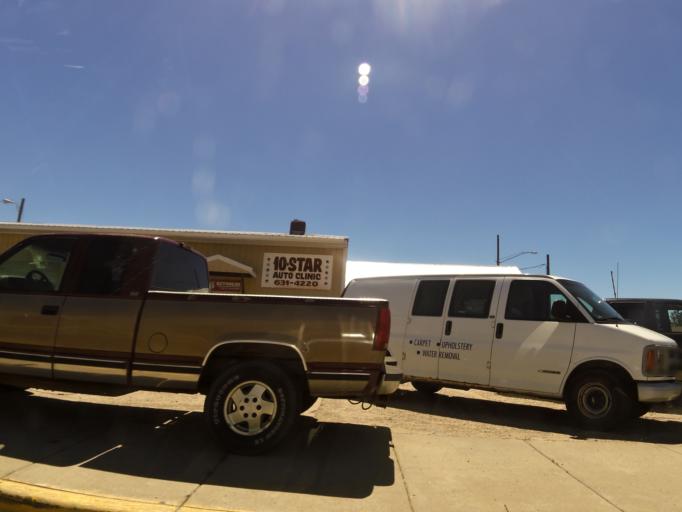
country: US
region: Minnesota
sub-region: Wadena County
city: Wadena
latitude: 46.4431
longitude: -95.1387
